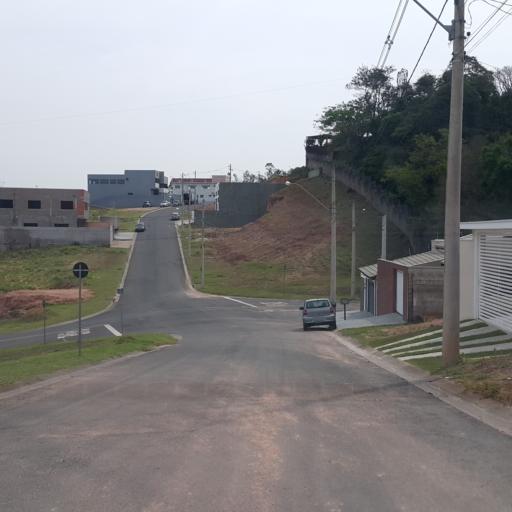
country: BR
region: Sao Paulo
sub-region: Louveira
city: Louveira
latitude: -23.0737
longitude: -46.9493
